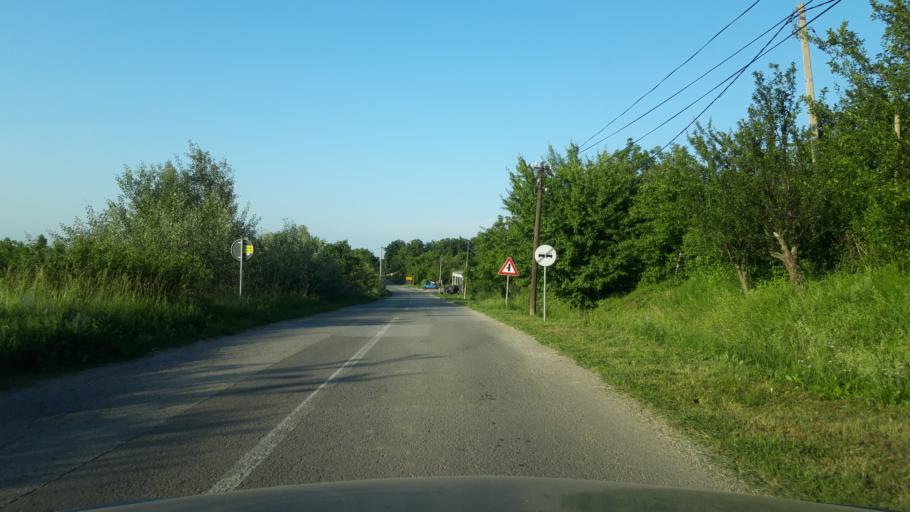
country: RS
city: Glozan
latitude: 45.2065
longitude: 19.5961
